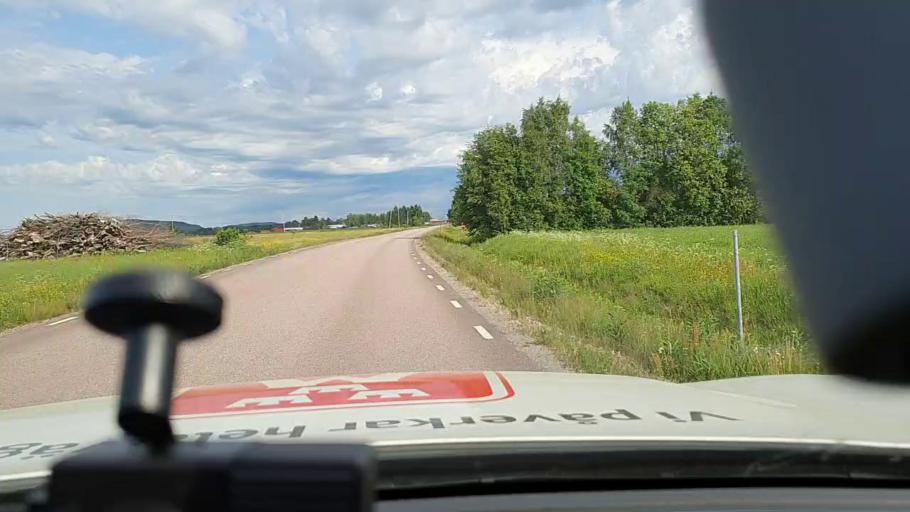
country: SE
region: Norrbotten
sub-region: Bodens Kommun
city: Saevast
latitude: 65.6992
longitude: 21.7733
